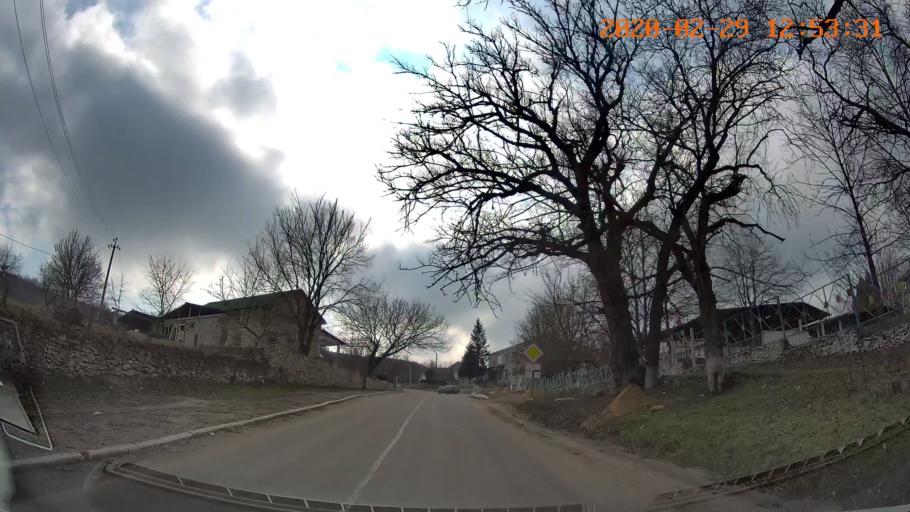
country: MD
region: Telenesti
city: Camenca
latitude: 48.1057
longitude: 28.7336
